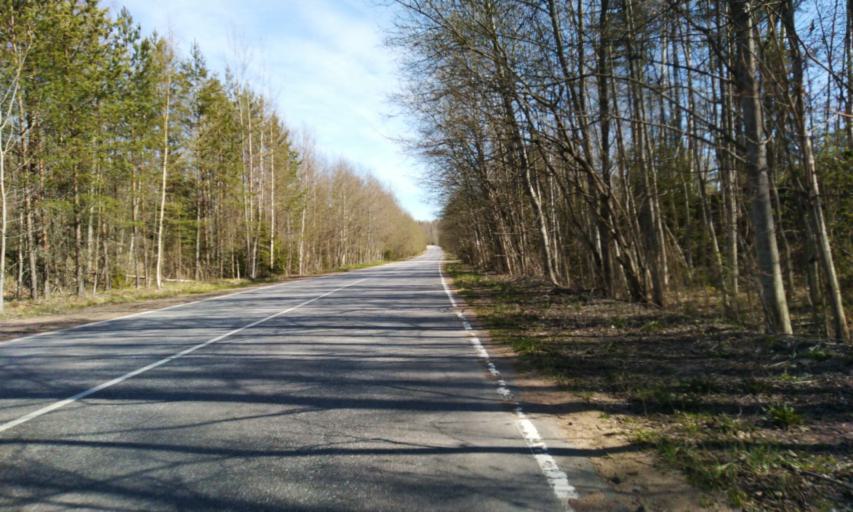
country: RU
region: Leningrad
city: Garbolovo
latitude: 60.4191
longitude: 30.4605
